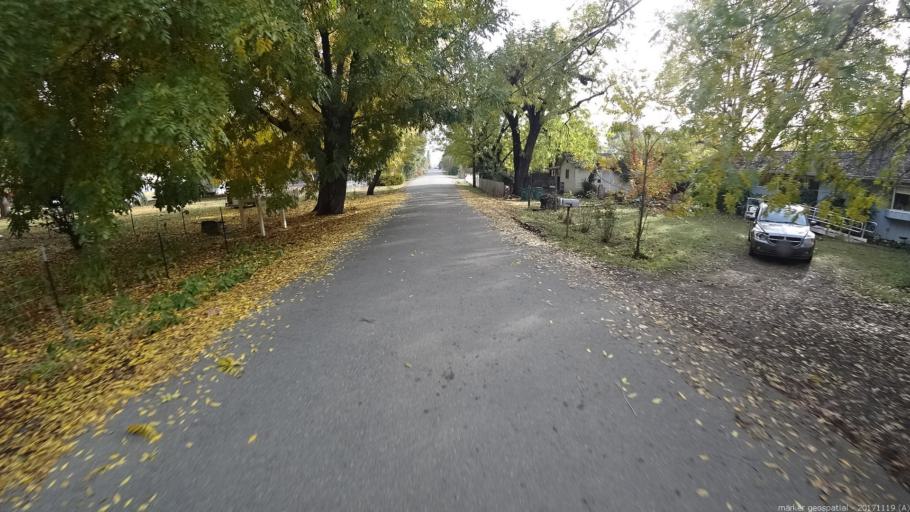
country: US
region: California
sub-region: Shasta County
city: Anderson
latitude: 40.5148
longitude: -122.3405
